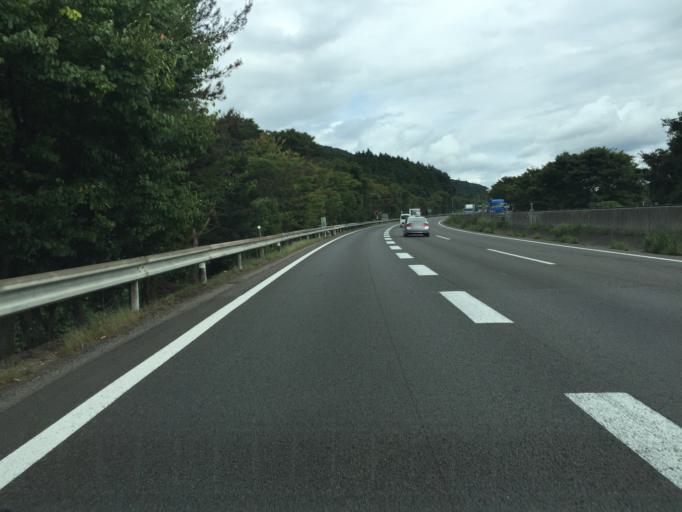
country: JP
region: Fukushima
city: Yanagawamachi-saiwaicho
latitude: 37.9015
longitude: 140.5700
